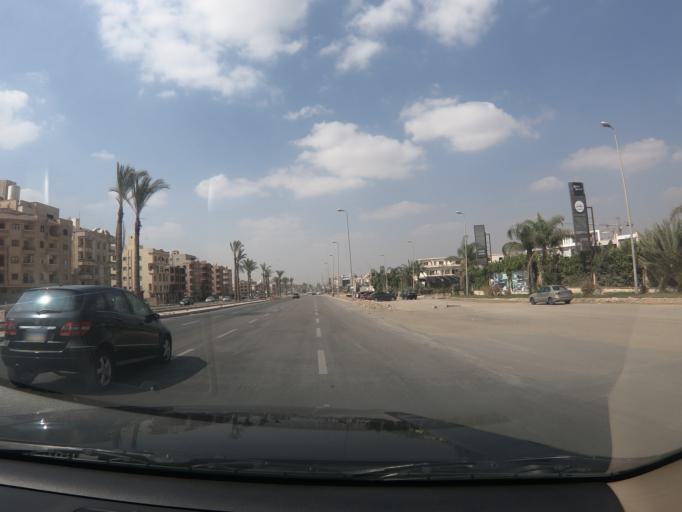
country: EG
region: Muhafazat al Qalyubiyah
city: Al Khankah
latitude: 30.0328
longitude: 31.4749
